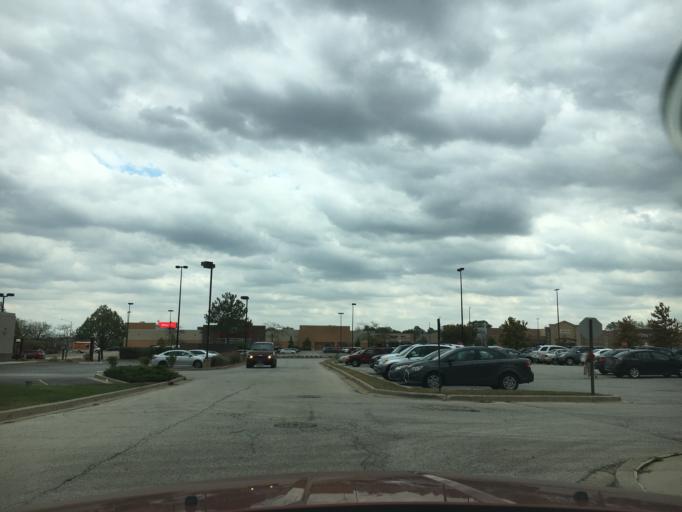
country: US
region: Illinois
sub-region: Cook County
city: Orland Hills
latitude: 41.6005
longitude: -87.8466
